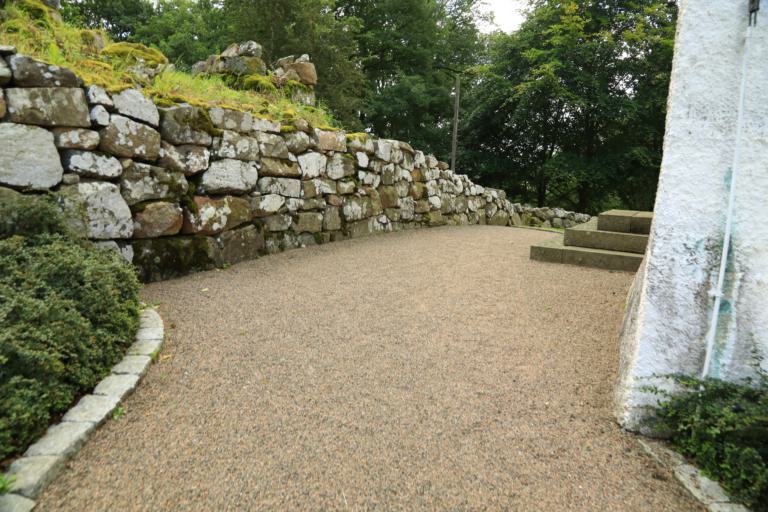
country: SE
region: Halland
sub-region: Varbergs Kommun
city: Tvaaker
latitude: 57.1439
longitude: 12.4681
